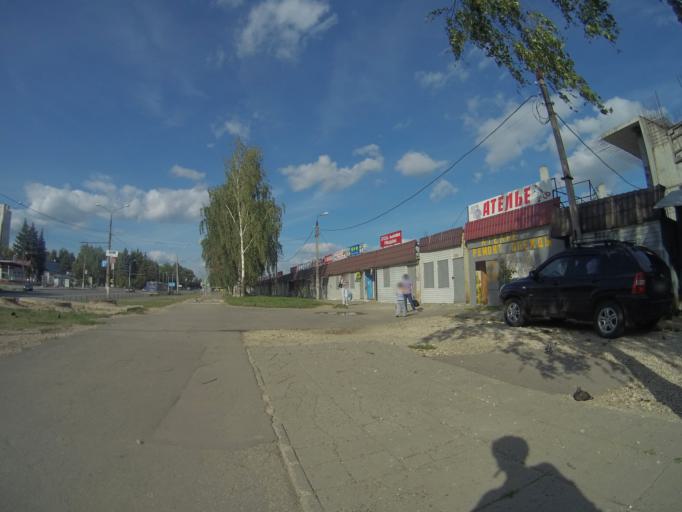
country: RU
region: Vladimir
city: Vladimir
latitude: 56.1397
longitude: 40.3654
